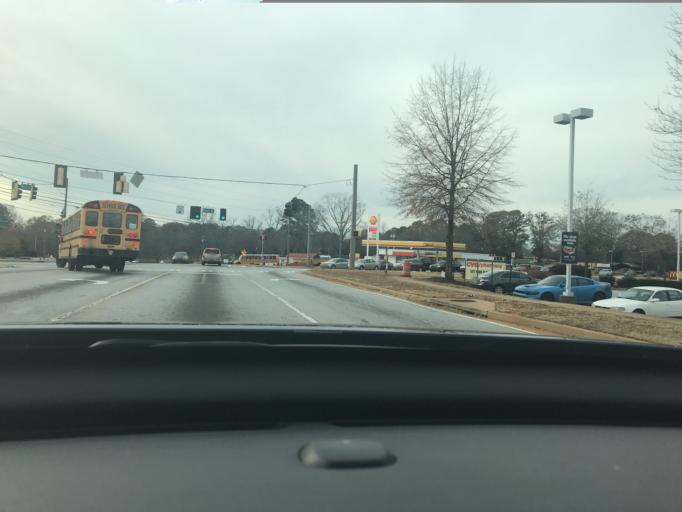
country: US
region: Georgia
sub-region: Newton County
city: Oakwood
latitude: 33.5786
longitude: -83.9632
